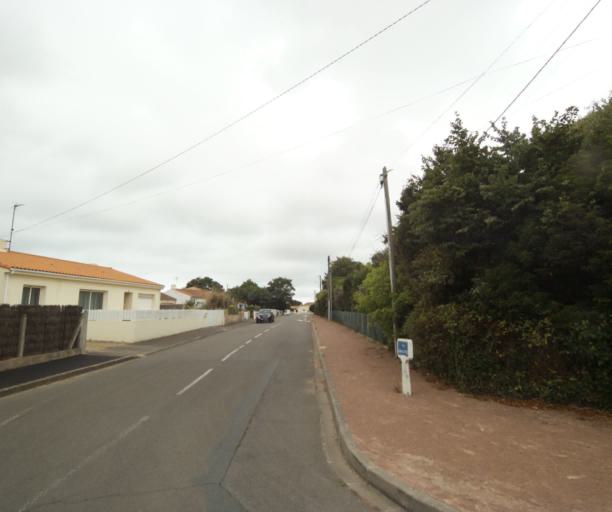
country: FR
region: Pays de la Loire
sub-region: Departement de la Vendee
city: Chateau-d'Olonne
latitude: 46.5022
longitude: -1.7503
